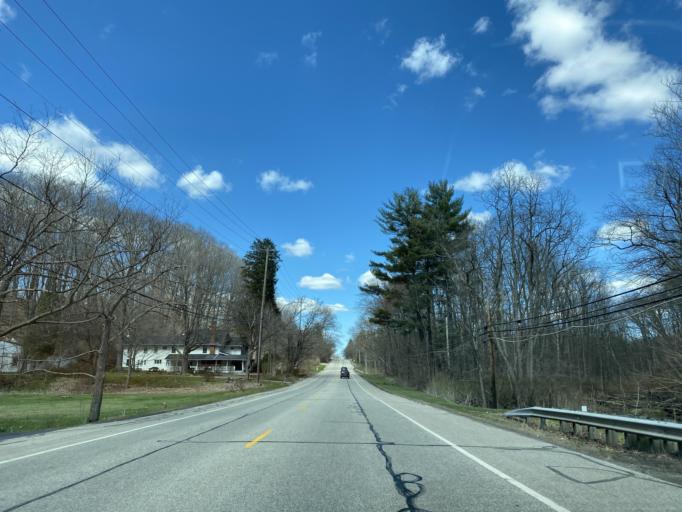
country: US
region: Ohio
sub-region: Summit County
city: Montrose-Ghent
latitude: 41.1631
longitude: -81.6368
